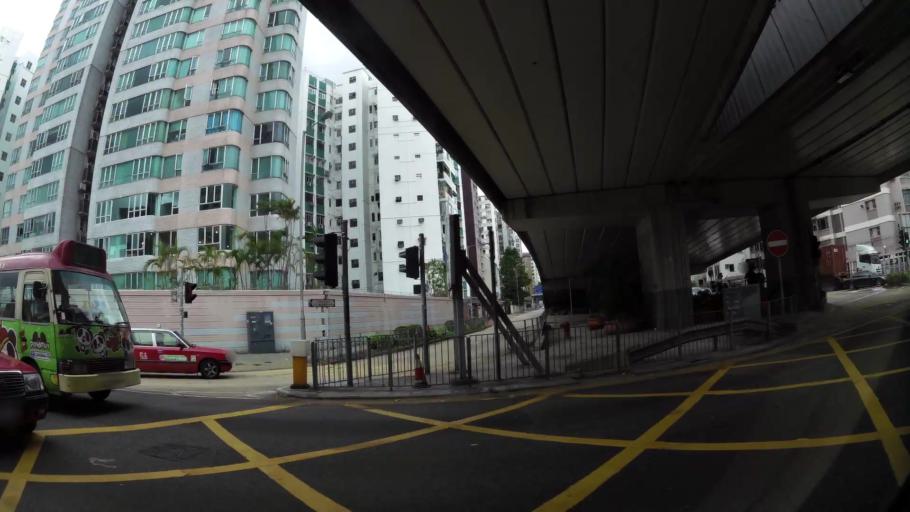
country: HK
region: Kowloon City
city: Kowloon
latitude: 22.3258
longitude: 114.1785
